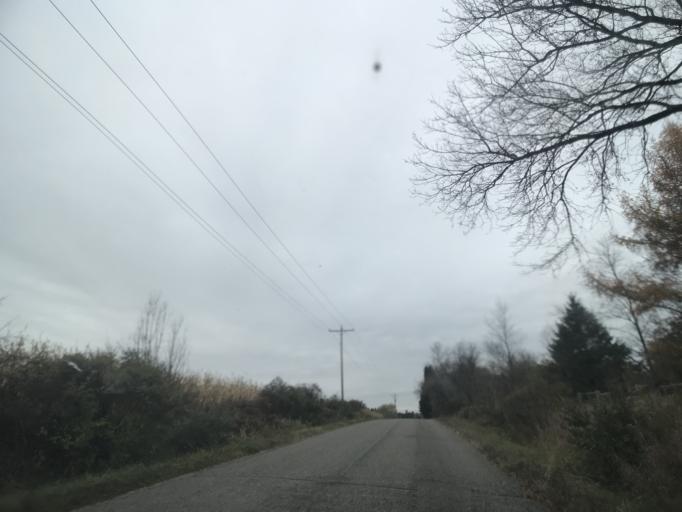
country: US
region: Wisconsin
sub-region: Menominee County
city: Legend Lake
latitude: 45.1812
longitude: -88.4622
